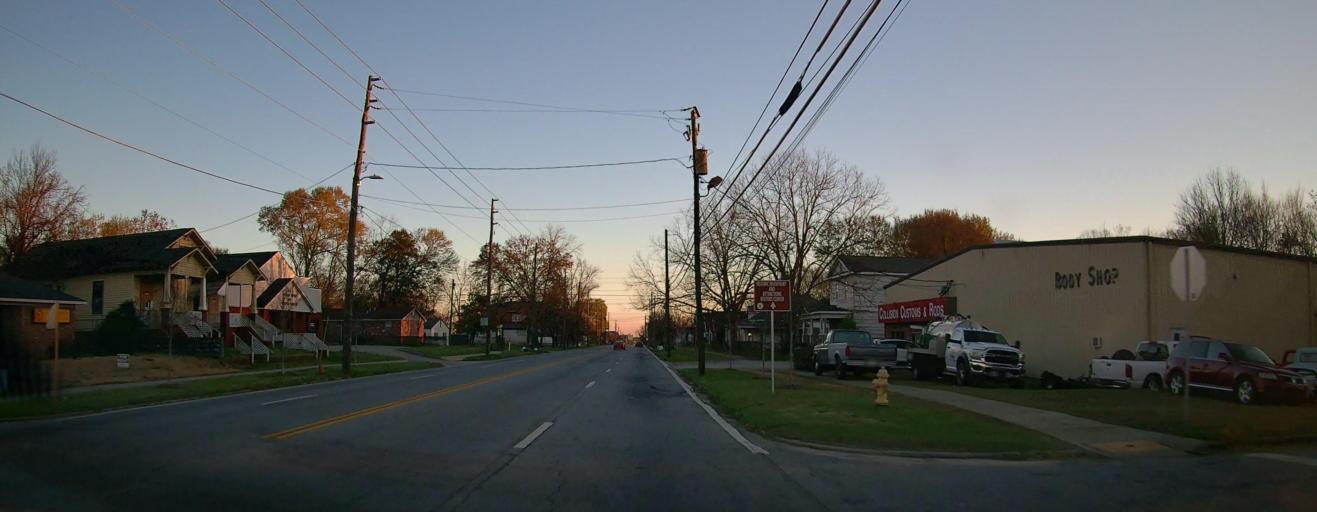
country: US
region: Alabama
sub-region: Russell County
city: Phenix City
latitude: 32.4899
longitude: -84.9902
